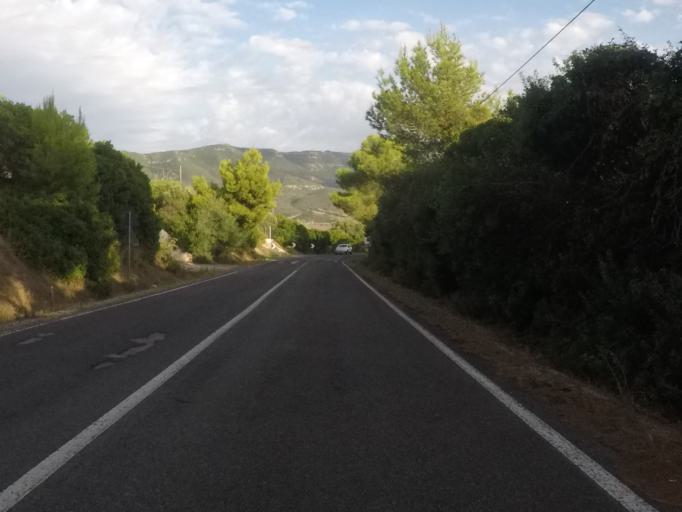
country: IT
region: Sardinia
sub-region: Provincia di Sassari
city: Alghero
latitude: 40.5121
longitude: 8.3543
